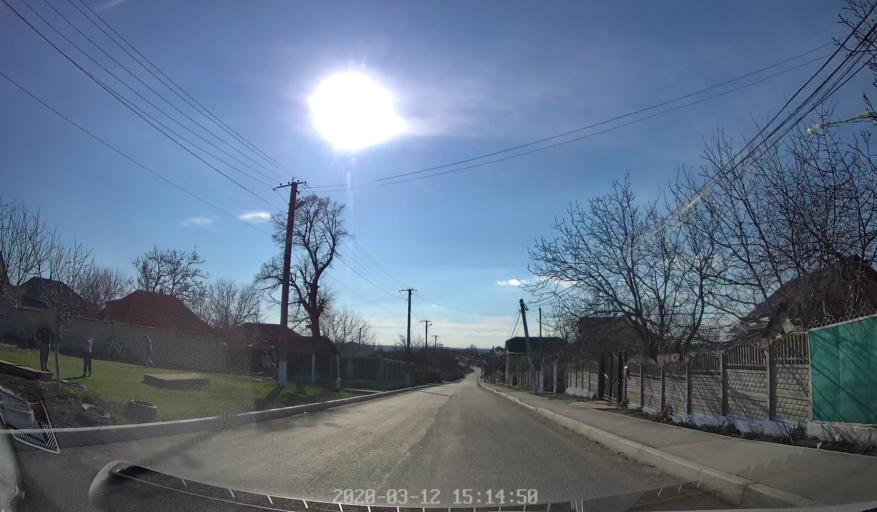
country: MD
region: Chisinau
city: Ciorescu
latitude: 47.2339
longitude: 28.9462
